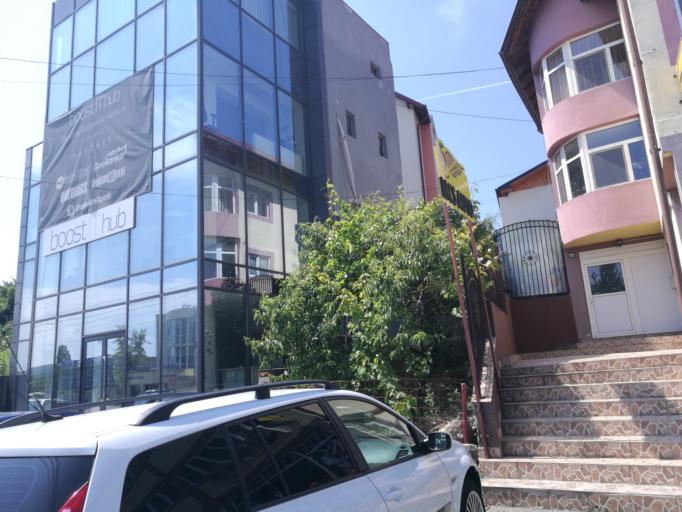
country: RO
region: Arges
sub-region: Comuna Bradu
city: Geamana
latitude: 44.8416
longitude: 24.8946
